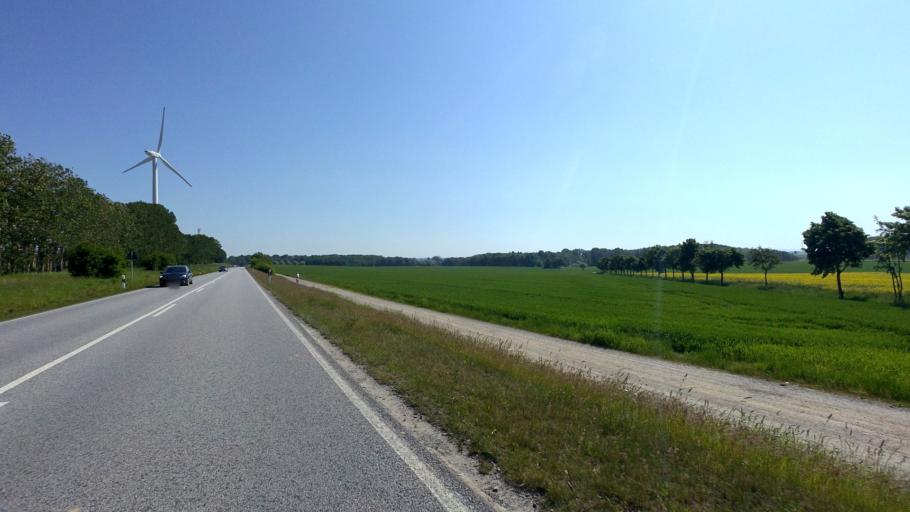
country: DE
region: Saxony
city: Elstra
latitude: 51.2344
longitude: 14.1553
